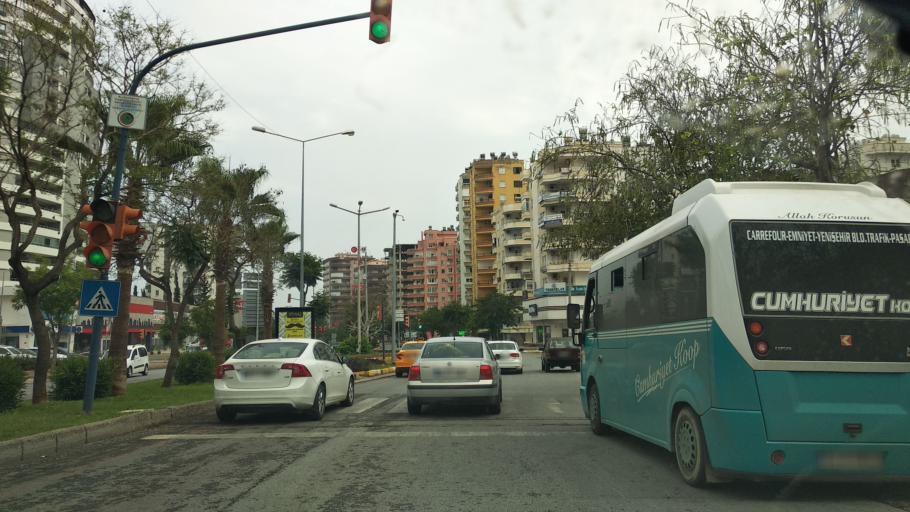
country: TR
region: Mersin
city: Mercin
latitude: 36.7990
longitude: 34.5949
